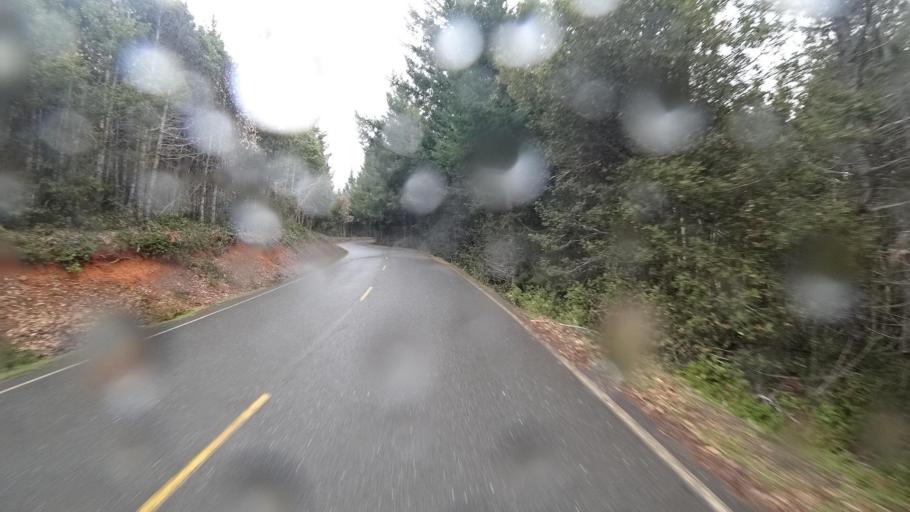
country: US
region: California
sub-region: Humboldt County
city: Willow Creek
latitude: 41.1919
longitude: -123.8143
